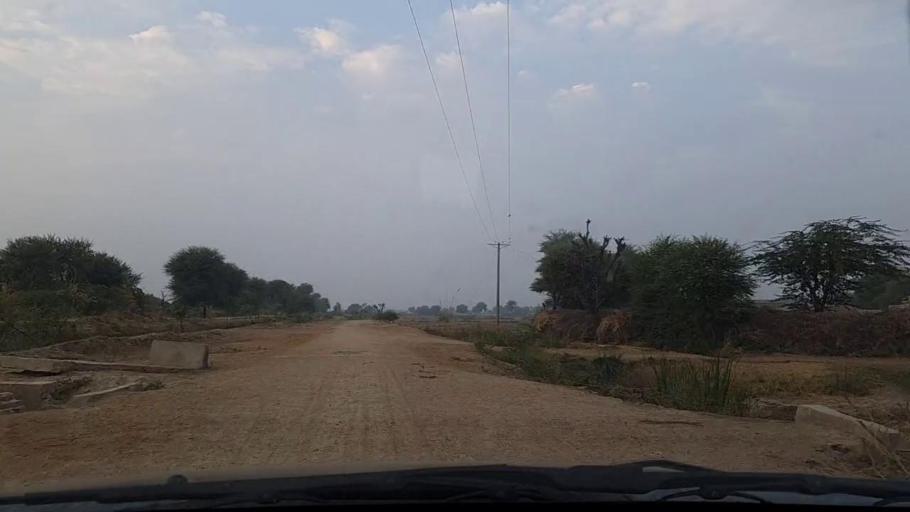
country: PK
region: Sindh
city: Pithoro
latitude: 25.6019
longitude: 69.4594
